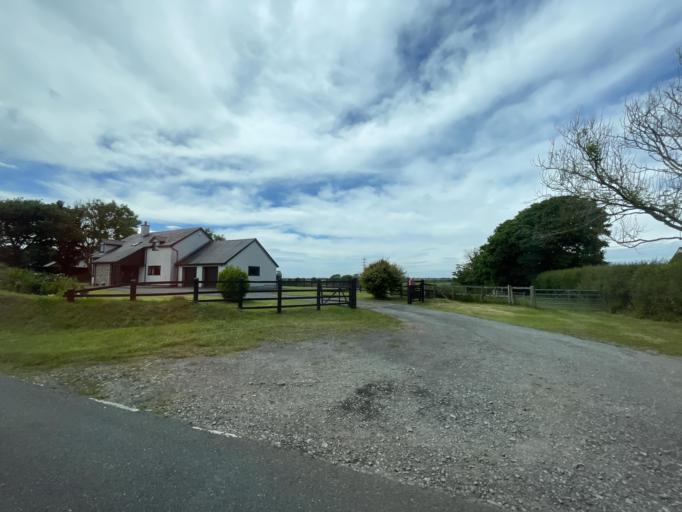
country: GB
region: Wales
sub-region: Anglesey
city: Gaerwen
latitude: 53.2158
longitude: -4.2465
